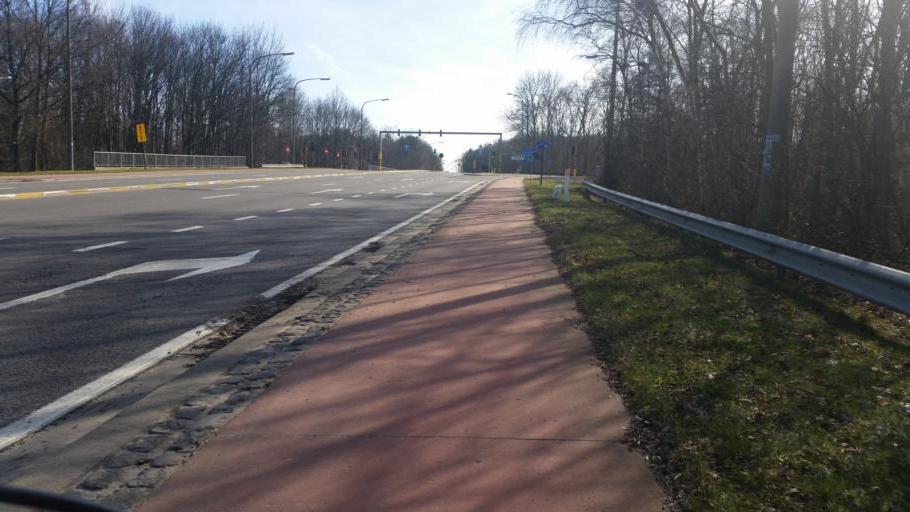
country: BE
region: Flanders
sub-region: Provincie Vlaams-Brabant
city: Wezembeek-Oppem
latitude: 50.8709
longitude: 4.5102
